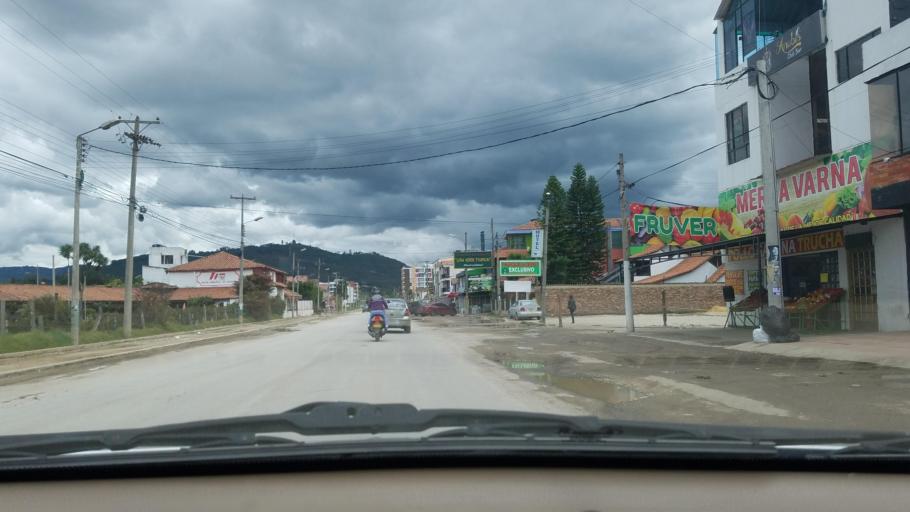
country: CO
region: Boyaca
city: Paipa
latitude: 5.7734
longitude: -73.1166
